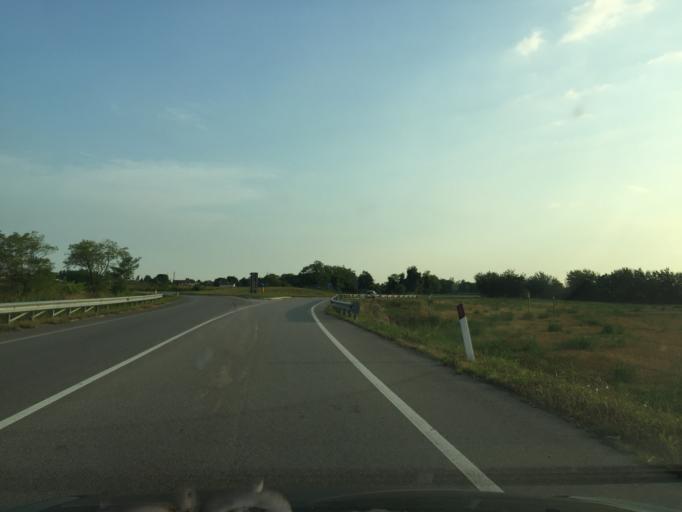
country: IT
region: Friuli Venezia Giulia
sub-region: Provincia di Udine
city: Manzano
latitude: 45.9787
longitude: 13.3780
